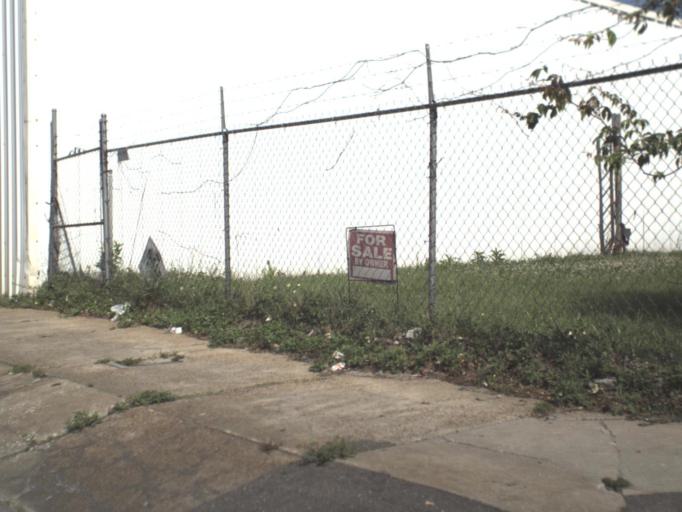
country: US
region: Florida
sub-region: Duval County
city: Jacksonville
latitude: 30.3319
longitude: -81.7046
